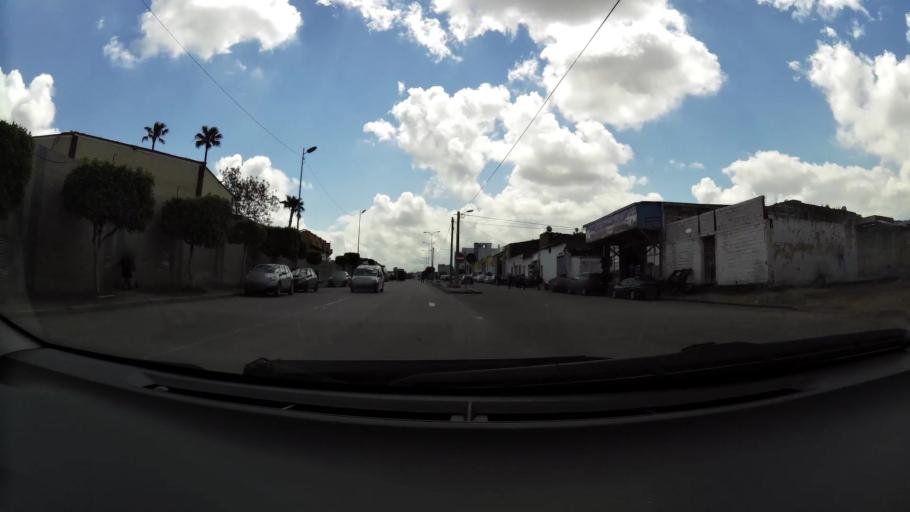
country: MA
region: Grand Casablanca
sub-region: Casablanca
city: Casablanca
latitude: 33.5419
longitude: -7.5596
